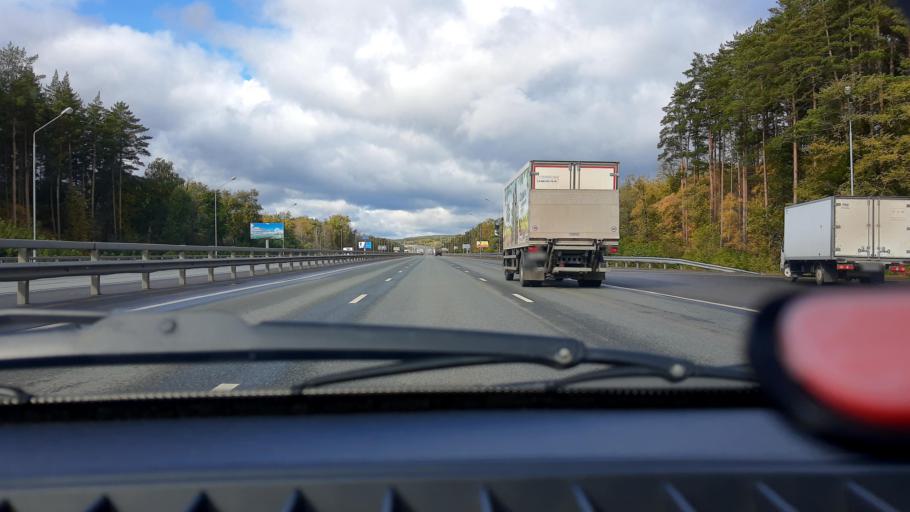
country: RU
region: Bashkortostan
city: Avdon
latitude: 54.6696
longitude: 55.8389
